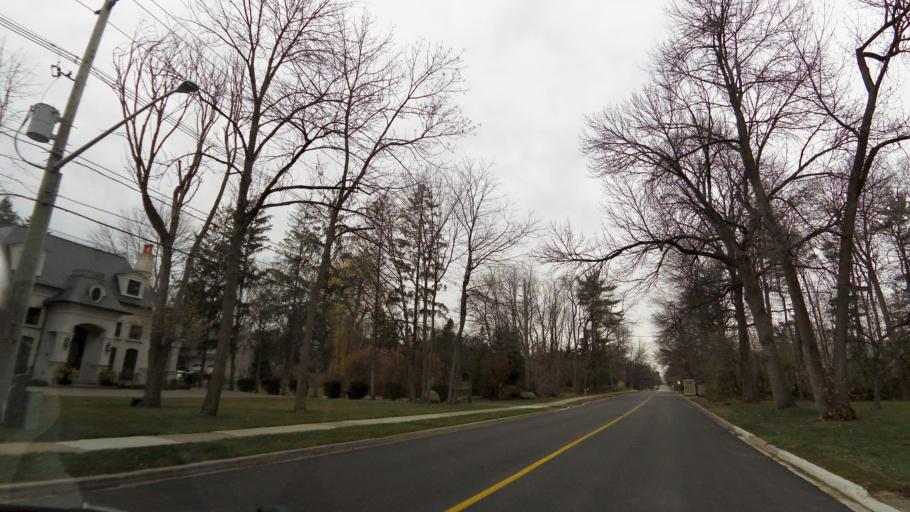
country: CA
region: Ontario
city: Oakville
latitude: 43.4696
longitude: -79.6444
